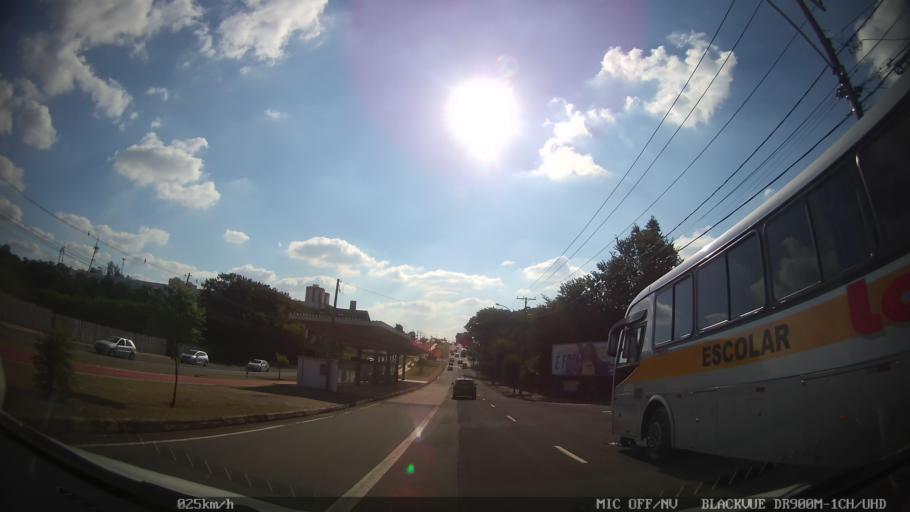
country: BR
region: Sao Paulo
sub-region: Nova Odessa
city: Nova Odessa
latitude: -22.7800
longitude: -47.3053
